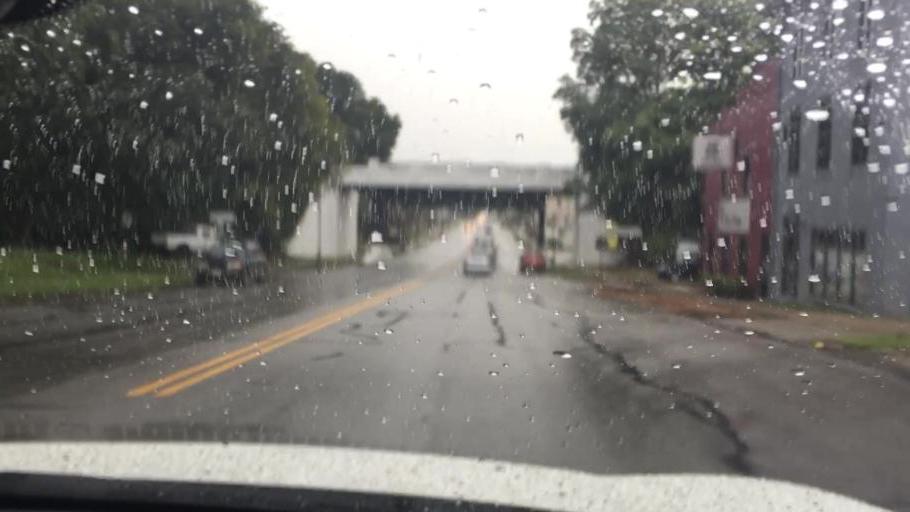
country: US
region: Ohio
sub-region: Champaign County
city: Urbana
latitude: 40.1084
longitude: -83.7570
